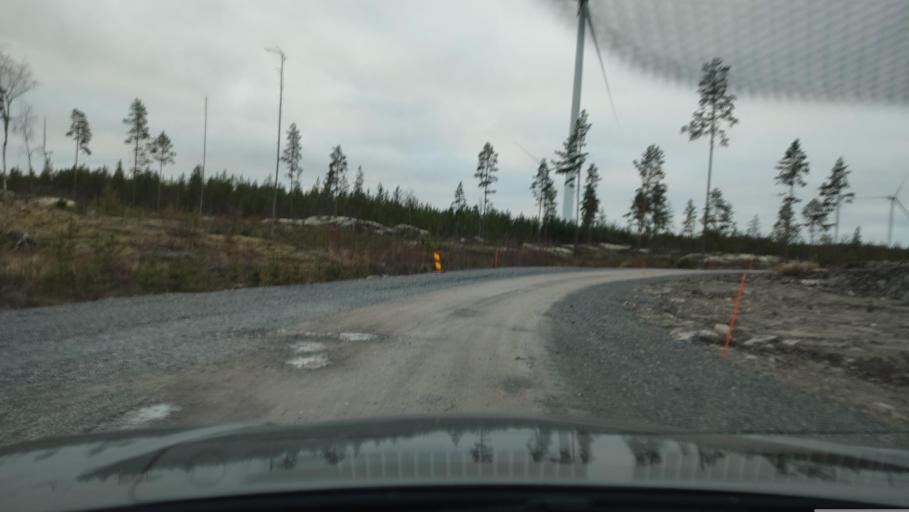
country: FI
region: Southern Ostrobothnia
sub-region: Suupohja
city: Karijoki
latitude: 62.1902
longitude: 21.5750
